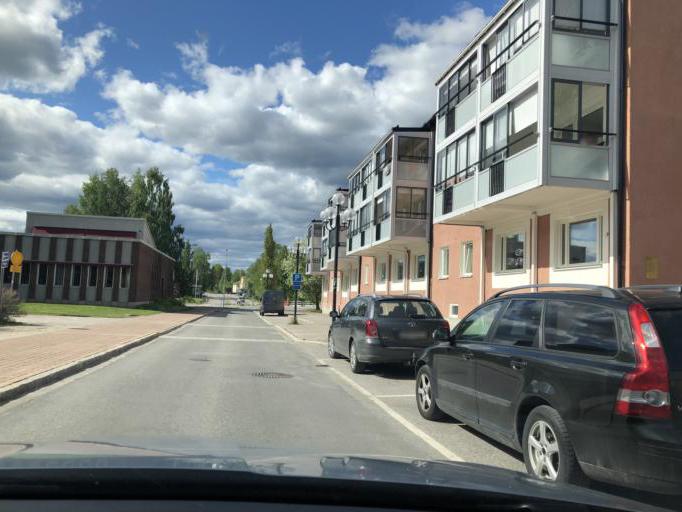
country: SE
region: Norrbotten
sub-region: Alvsbyns Kommun
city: AElvsbyn
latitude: 65.6742
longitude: 21.0074
